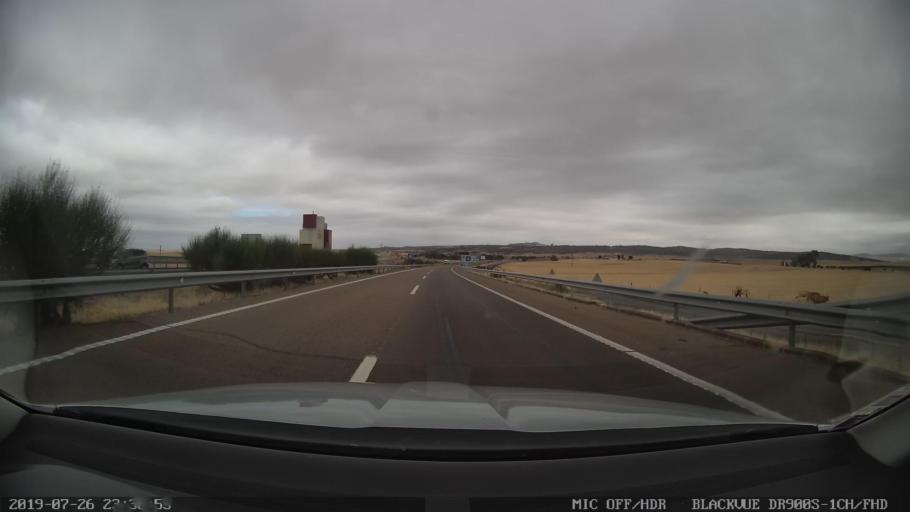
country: ES
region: Extremadura
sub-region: Provincia de Caceres
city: Trujillo
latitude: 39.4026
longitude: -5.8895
